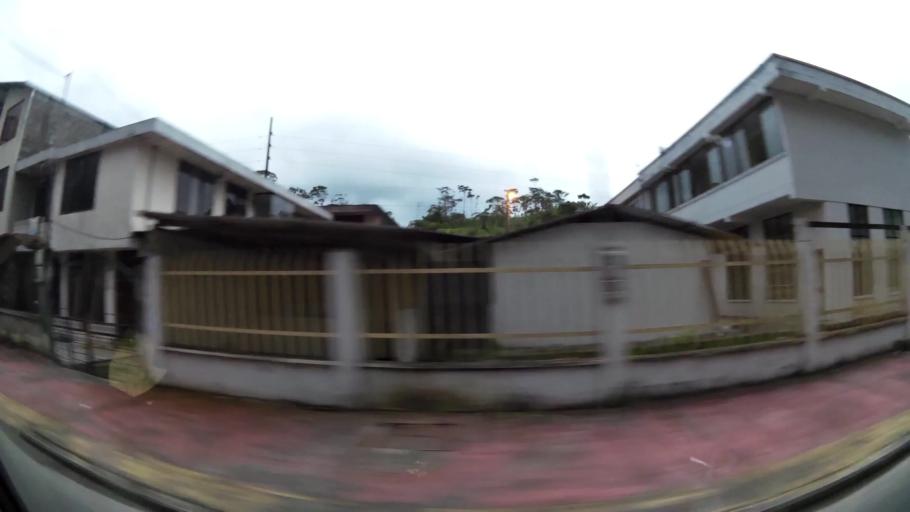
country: EC
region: Pastaza
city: Puyo
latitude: -1.4811
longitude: -78.0093
